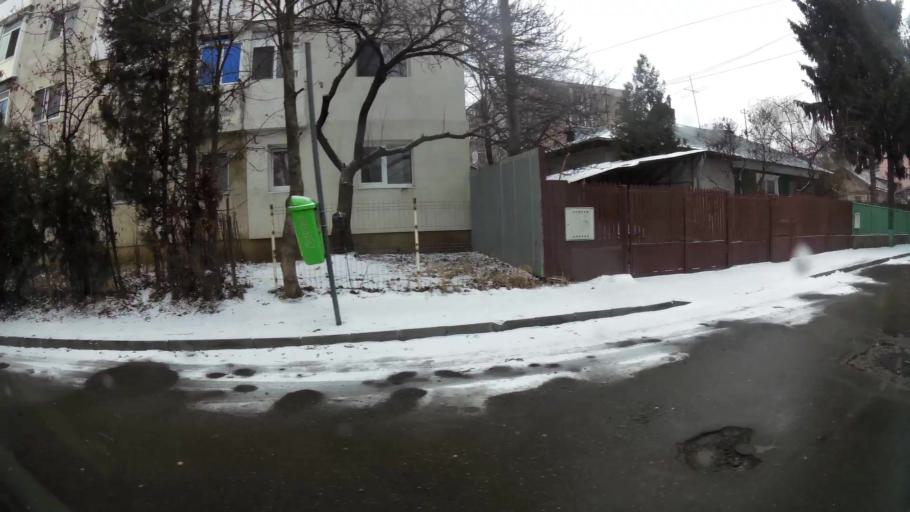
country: RO
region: Prahova
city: Ploiesti
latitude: 44.9394
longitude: 25.9961
